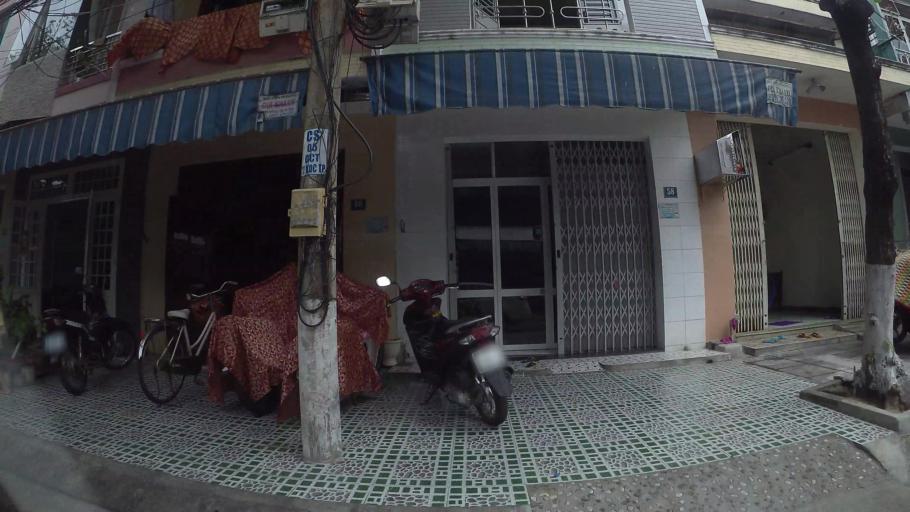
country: VN
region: Da Nang
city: Da Nang
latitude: 16.0887
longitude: 108.2184
